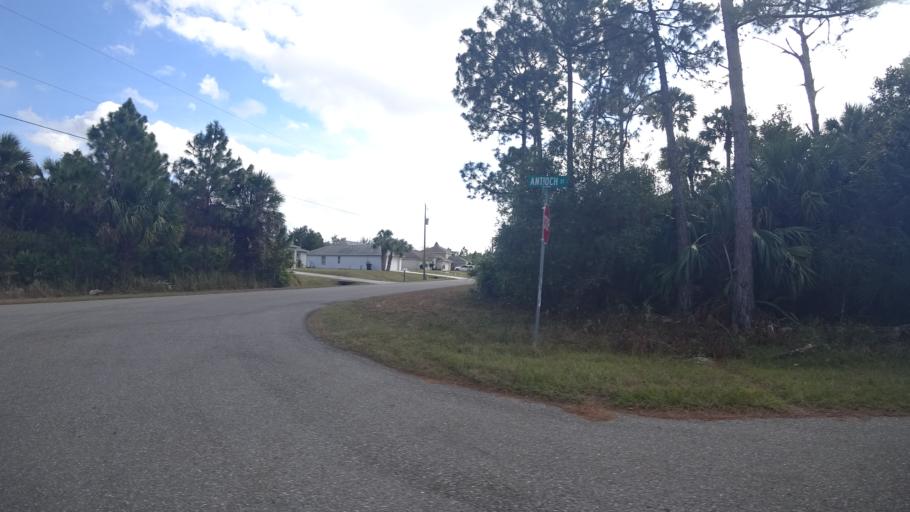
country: US
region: Florida
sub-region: Charlotte County
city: Port Charlotte
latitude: 27.0445
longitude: -82.1333
